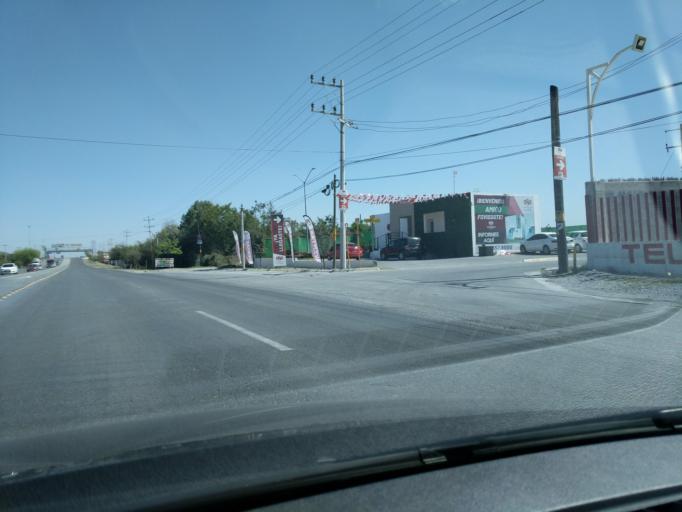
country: MX
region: Nuevo Leon
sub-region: Juarez
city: San Antonio
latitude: 25.6322
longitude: -100.0774
